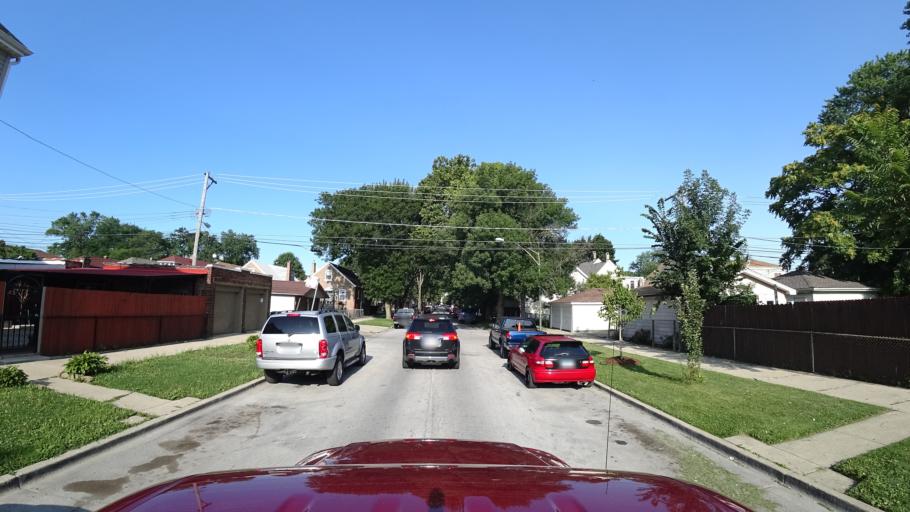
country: US
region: Illinois
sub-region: Cook County
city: Cicero
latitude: 41.7990
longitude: -87.7065
